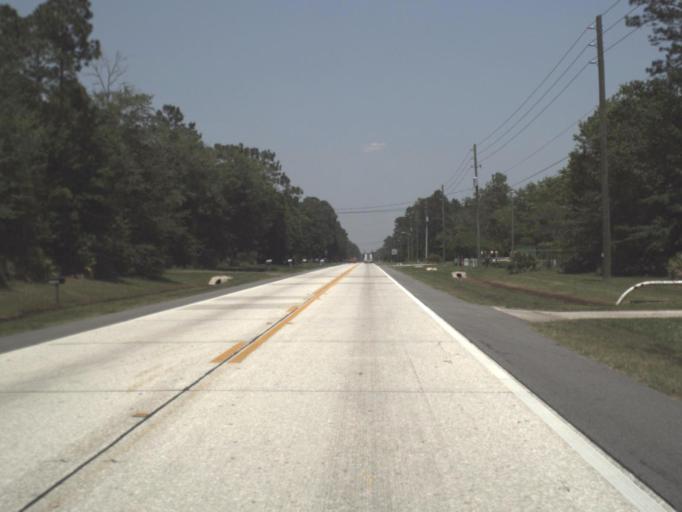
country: US
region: Florida
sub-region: Duval County
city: Baldwin
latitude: 30.2136
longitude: -81.9502
